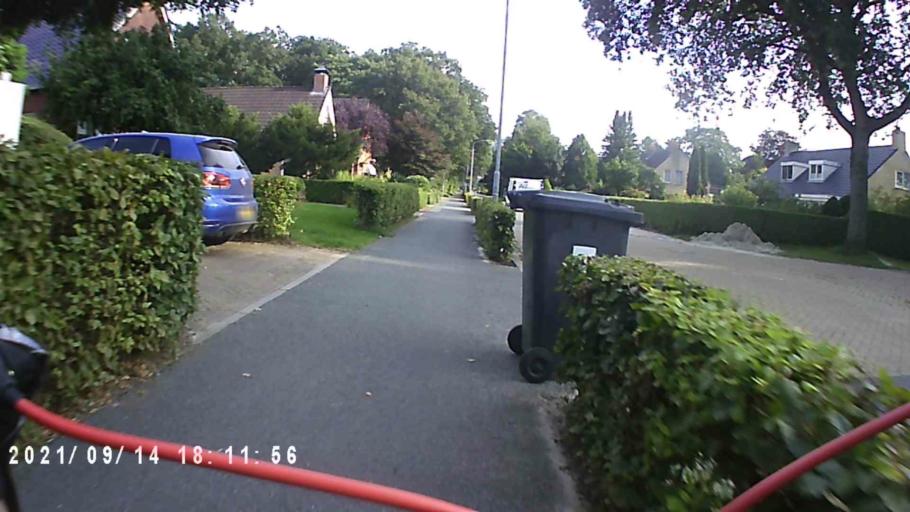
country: NL
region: Drenthe
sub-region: Gemeente Tynaarlo
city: Zuidlaren
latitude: 53.0915
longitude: 6.6623
